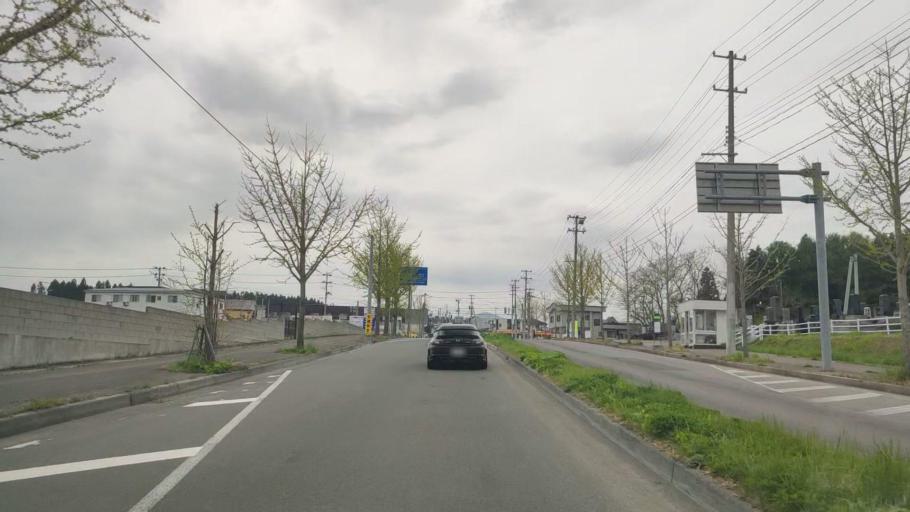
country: JP
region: Aomori
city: Aomori Shi
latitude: 40.7911
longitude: 140.7868
